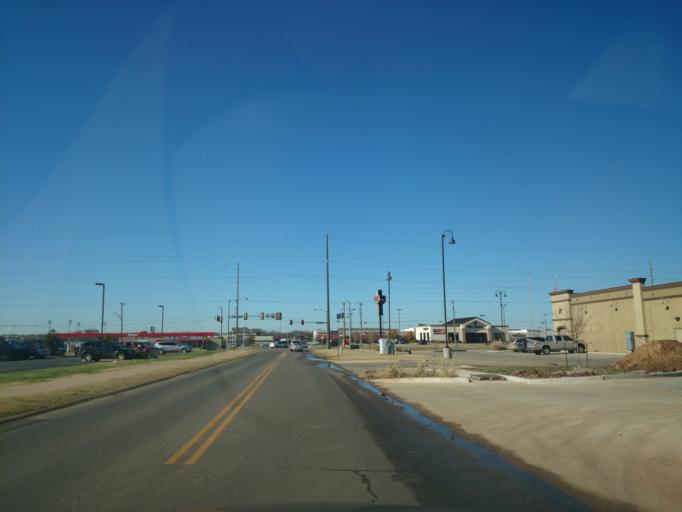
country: US
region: Oklahoma
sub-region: Payne County
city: Stillwater
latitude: 36.1407
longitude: -97.0503
